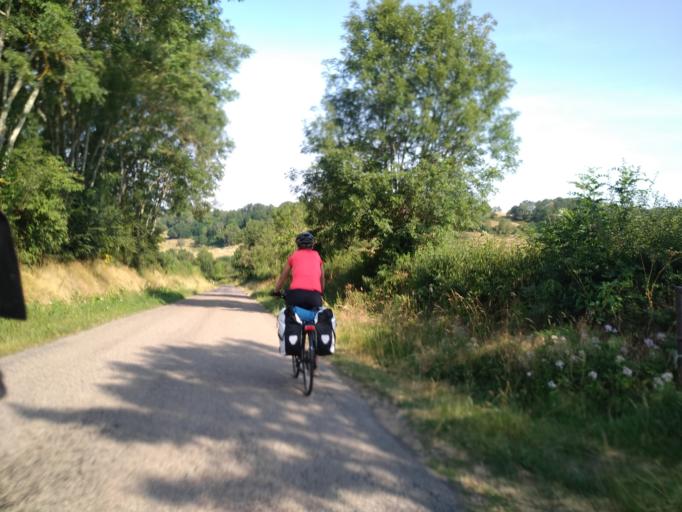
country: FR
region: Bourgogne
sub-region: Departement de Saone-et-Loire
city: Marcigny
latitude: 46.2592
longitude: 4.1077
